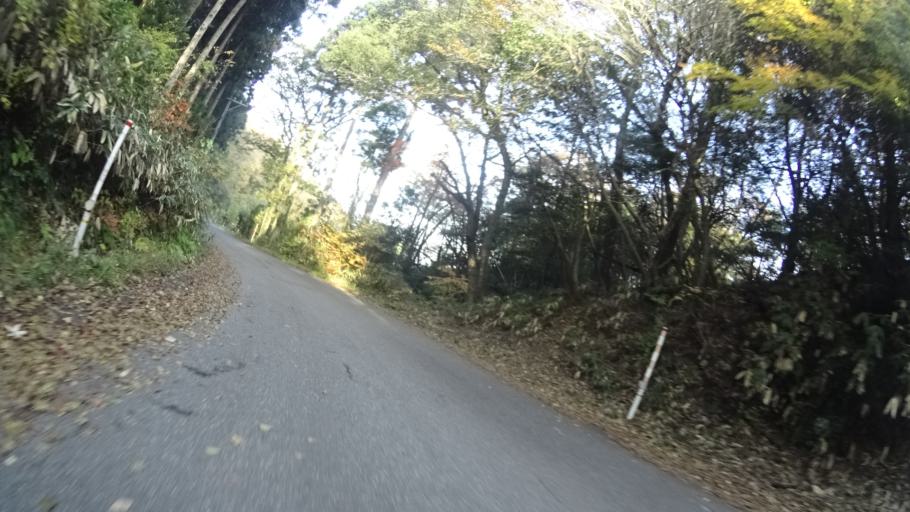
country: JP
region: Ishikawa
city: Nanao
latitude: 37.0187
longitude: 136.9858
